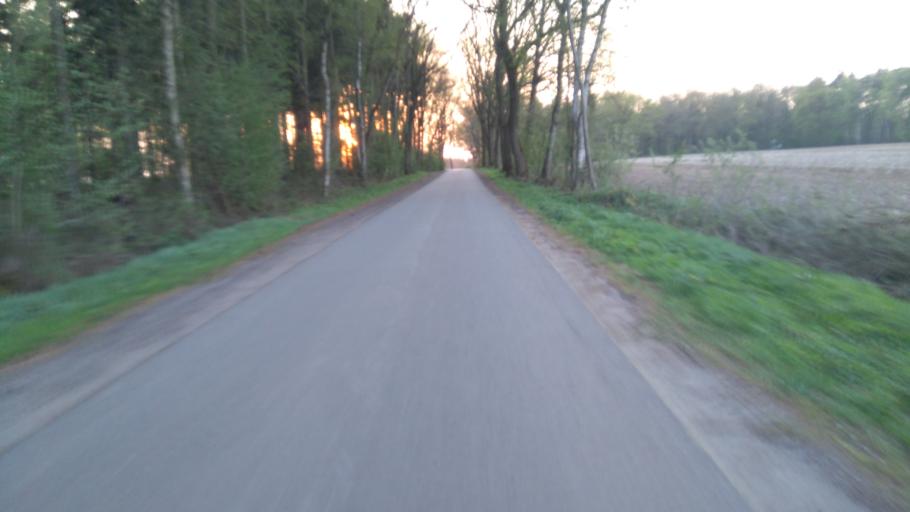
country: DE
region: Lower Saxony
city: Harsefeld
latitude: 53.4929
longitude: 9.4953
